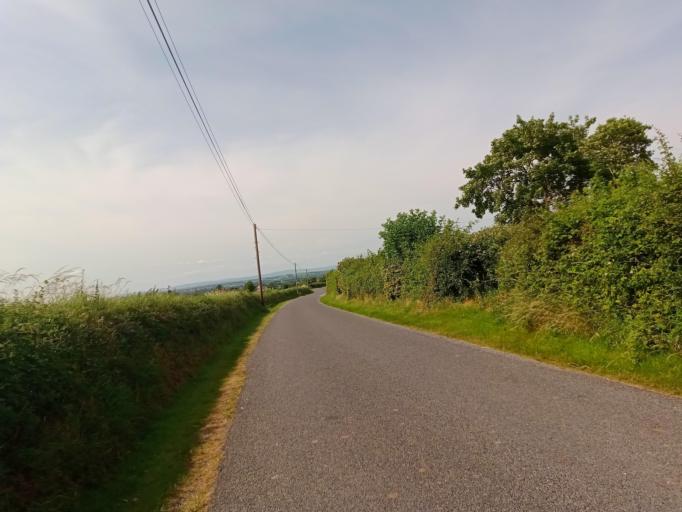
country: IE
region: Leinster
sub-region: Laois
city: Rathdowney
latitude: 52.8089
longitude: -7.4682
